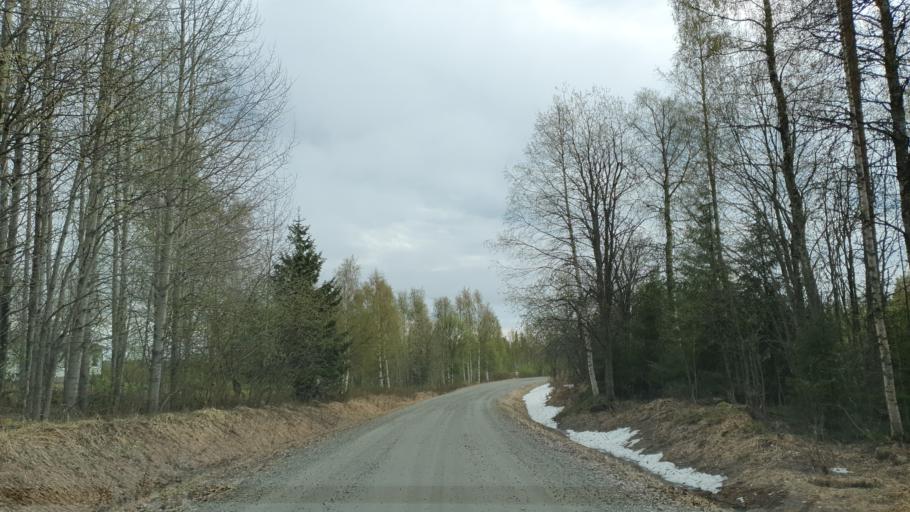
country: FI
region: Kainuu
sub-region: Kehys-Kainuu
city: Kuhmo
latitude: 64.1394
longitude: 29.9678
